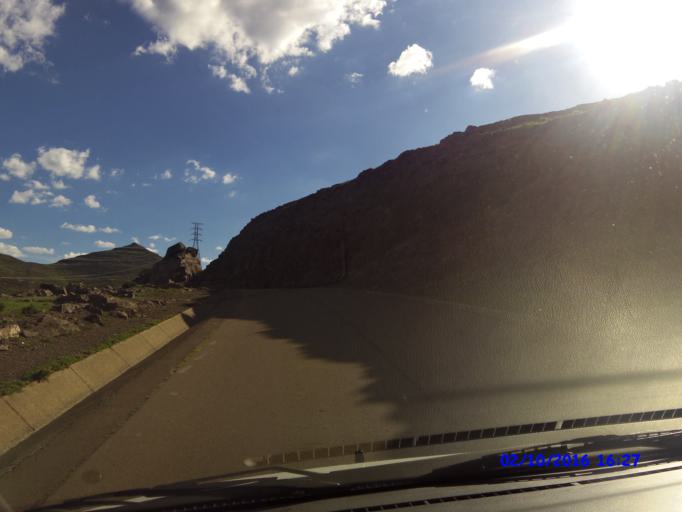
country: LS
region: Maseru
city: Nako
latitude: -29.4668
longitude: 28.0919
